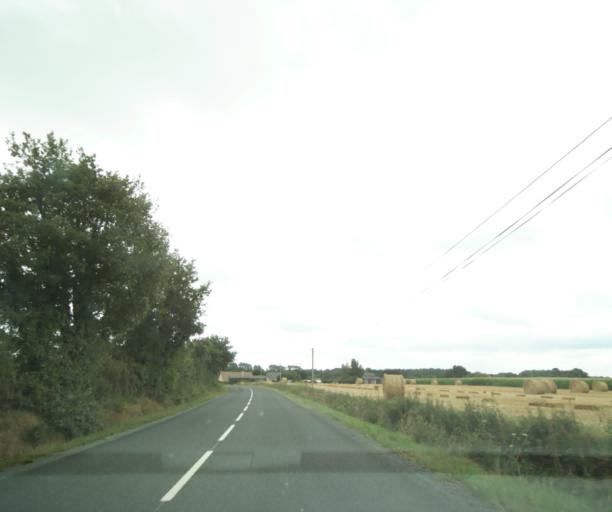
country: FR
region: Pays de la Loire
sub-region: Departement de Maine-et-Loire
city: Durtal
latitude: 47.7200
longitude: -0.2634
